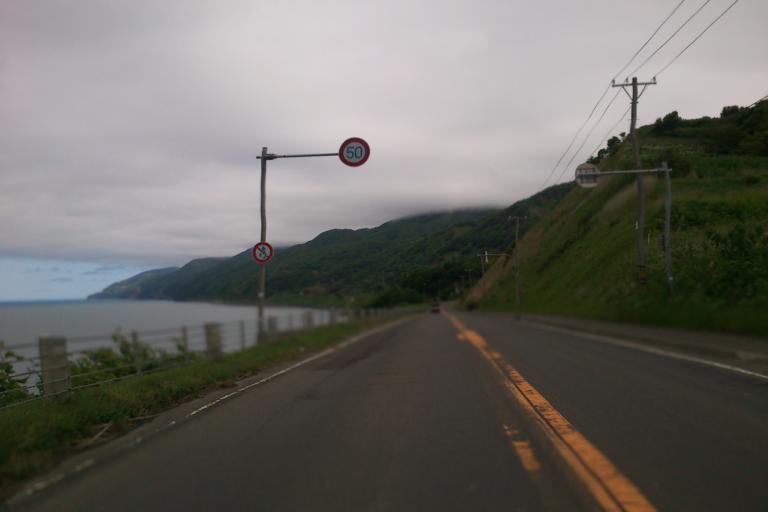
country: JP
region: Hokkaido
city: Ishikari
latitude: 43.4071
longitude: 141.4303
